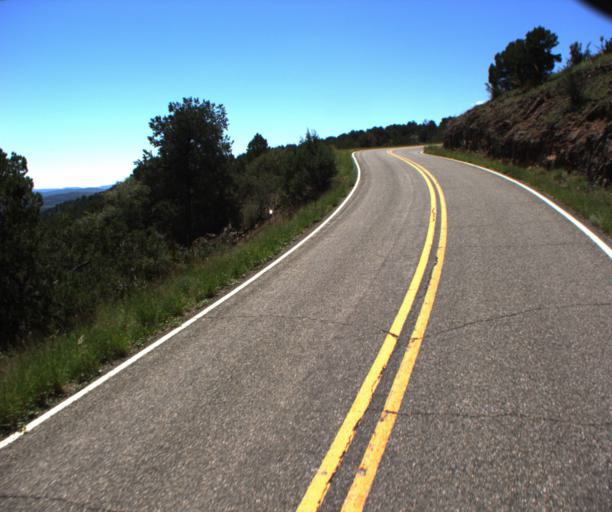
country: US
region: Arizona
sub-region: Greenlee County
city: Morenci
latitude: 33.3493
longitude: -109.3455
